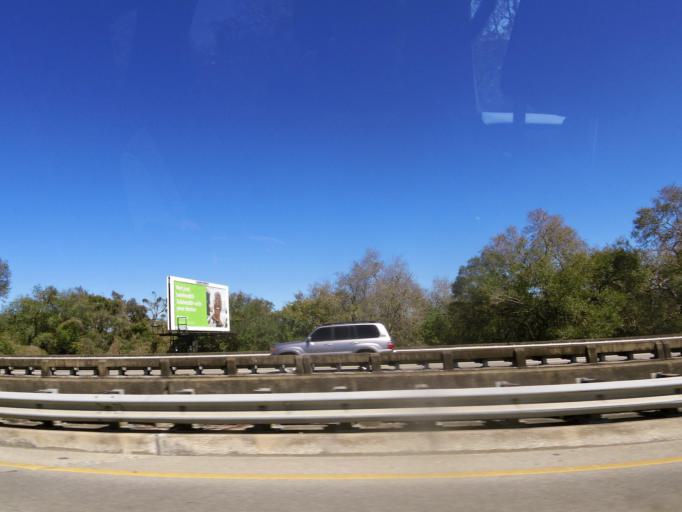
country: US
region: Florida
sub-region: Orange County
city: Lockhart
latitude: 28.6229
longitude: -81.4454
